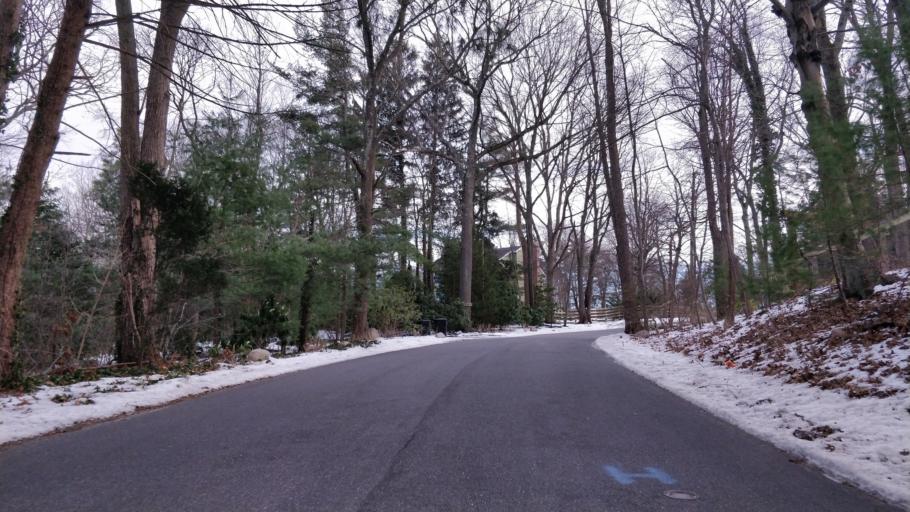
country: US
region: New York
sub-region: Suffolk County
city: Greenlawn
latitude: 40.8780
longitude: -73.3663
